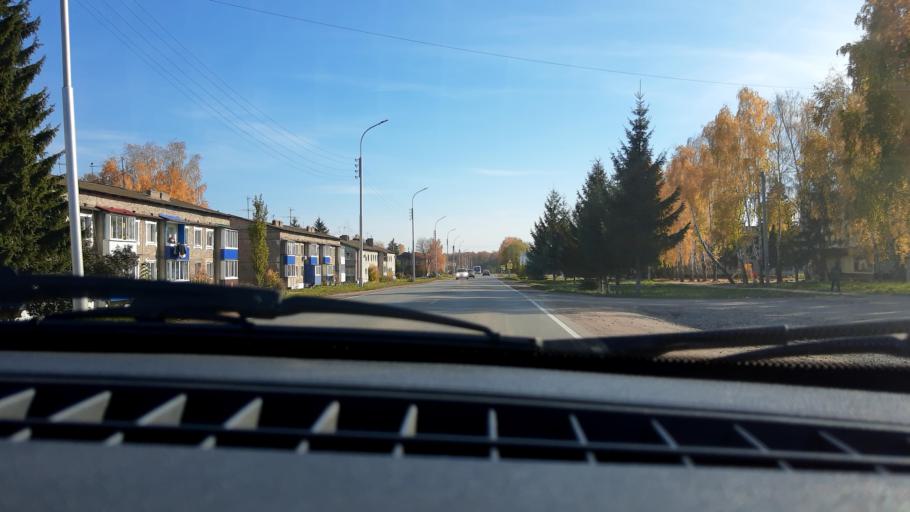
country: RU
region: Bashkortostan
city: Mikhaylovka
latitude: 54.8126
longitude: 55.8053
